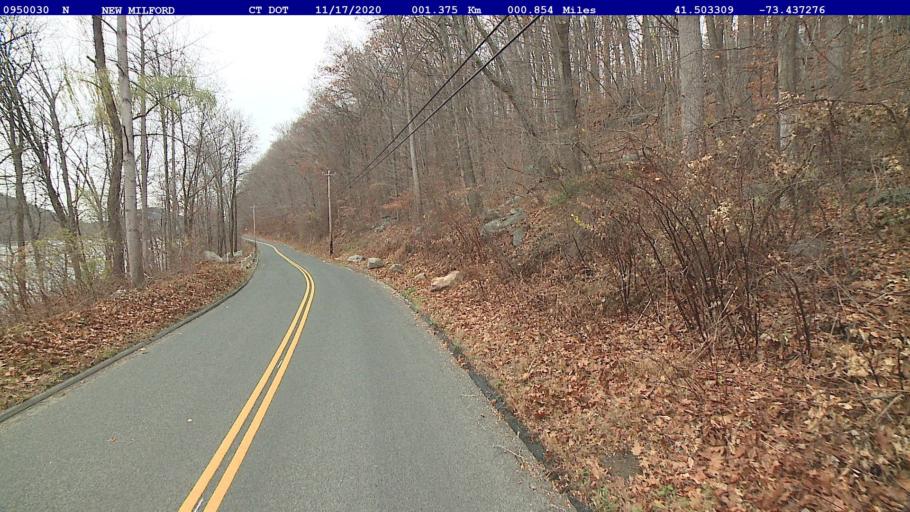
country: US
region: Connecticut
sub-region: Litchfield County
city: New Milford
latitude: 41.5033
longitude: -73.4373
